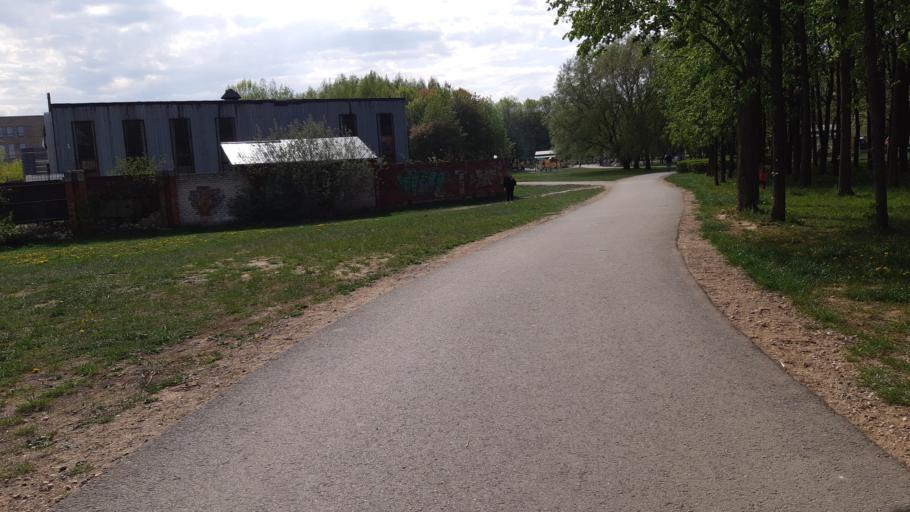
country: LT
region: Kauno apskritis
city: Dainava (Kaunas)
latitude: 54.9230
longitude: 23.9514
